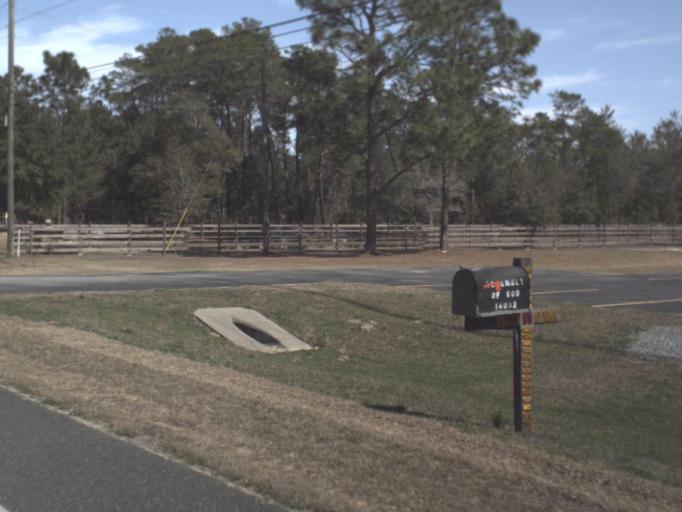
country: US
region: Florida
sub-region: Bay County
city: Lynn Haven
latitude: 30.4058
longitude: -85.6899
